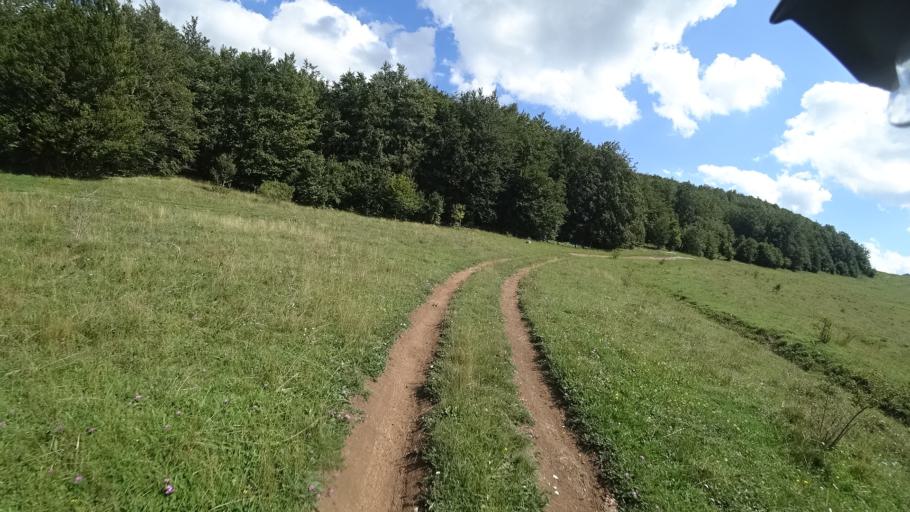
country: HR
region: Zadarska
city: Gracac
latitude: 44.4378
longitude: 15.9857
